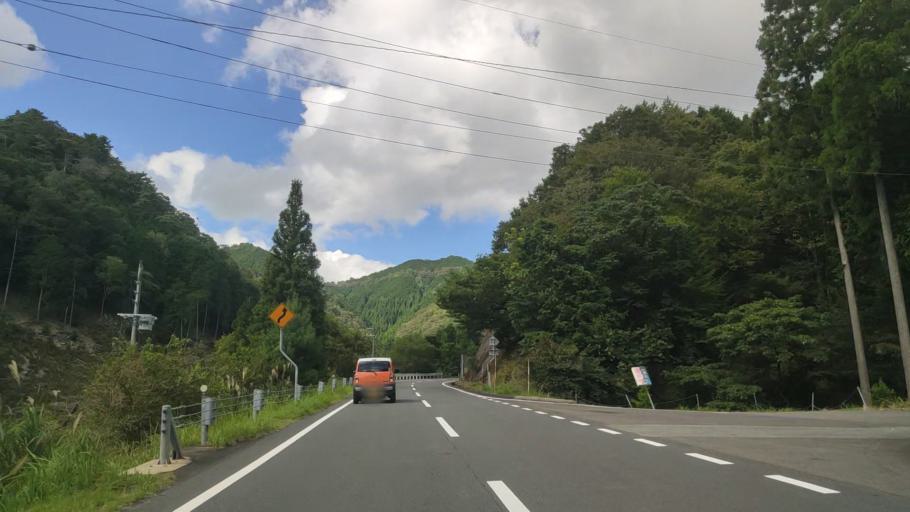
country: JP
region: Hyogo
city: Toyooka
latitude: 35.5184
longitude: 134.9898
